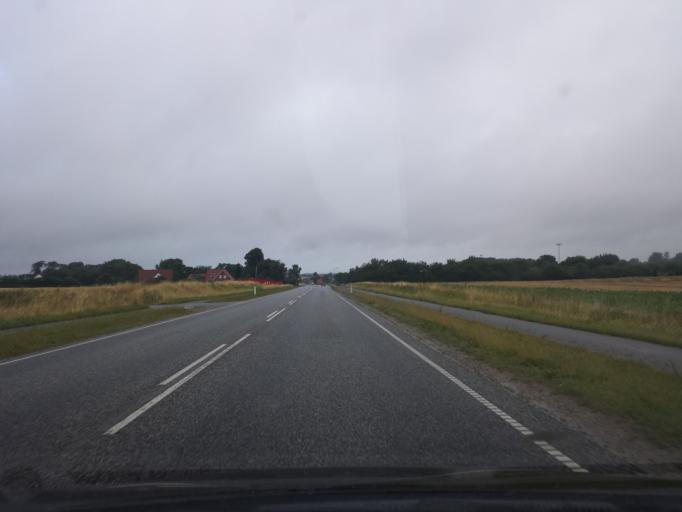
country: DK
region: South Denmark
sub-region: Sonderborg Kommune
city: Augustenborg
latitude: 54.9608
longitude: 9.8995
